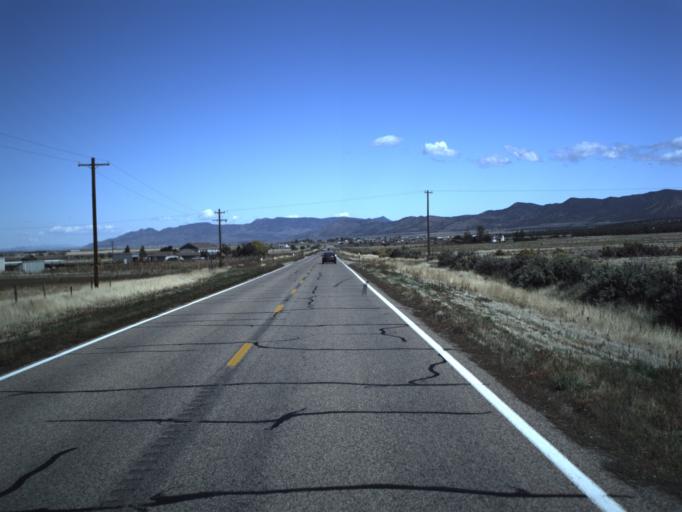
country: US
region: Utah
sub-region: Washington County
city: Enterprise
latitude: 37.5798
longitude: -113.6905
